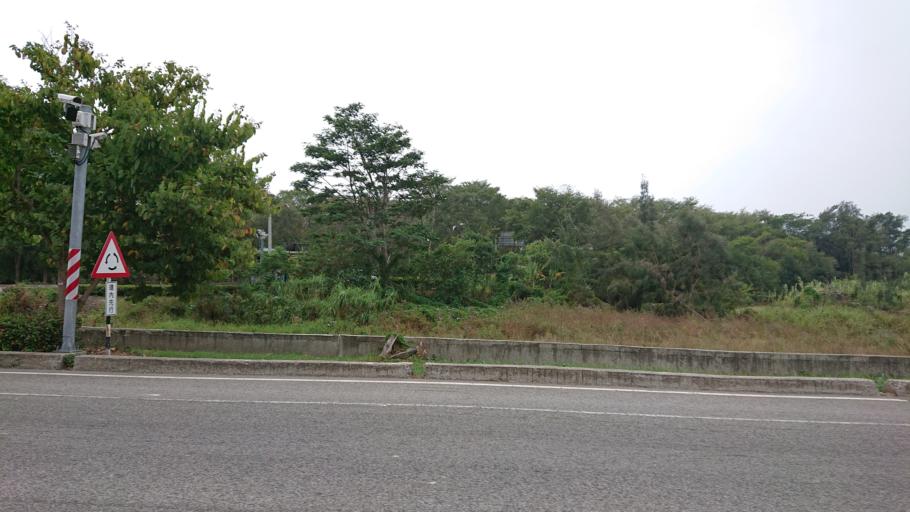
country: TW
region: Fukien
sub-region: Kinmen
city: Jincheng
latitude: 24.4477
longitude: 118.3848
